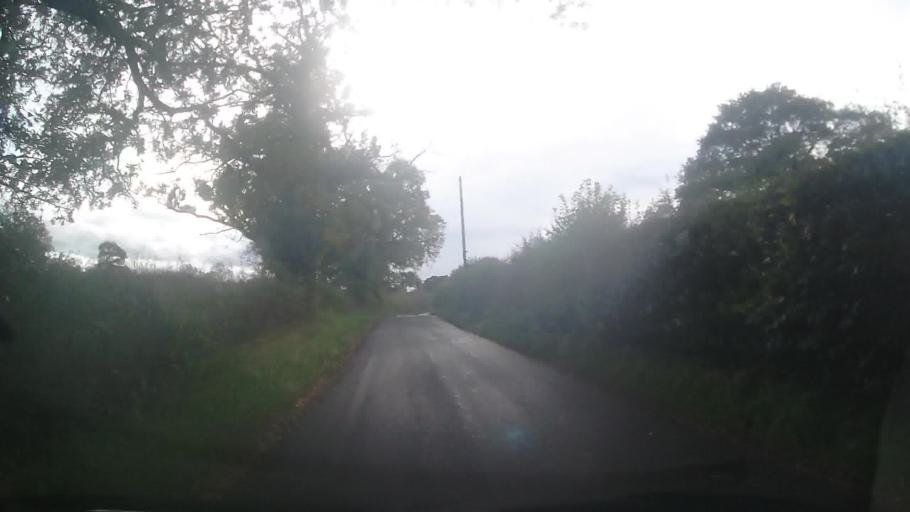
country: GB
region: England
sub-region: Shropshire
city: Whitchurch
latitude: 52.9364
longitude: -2.7215
